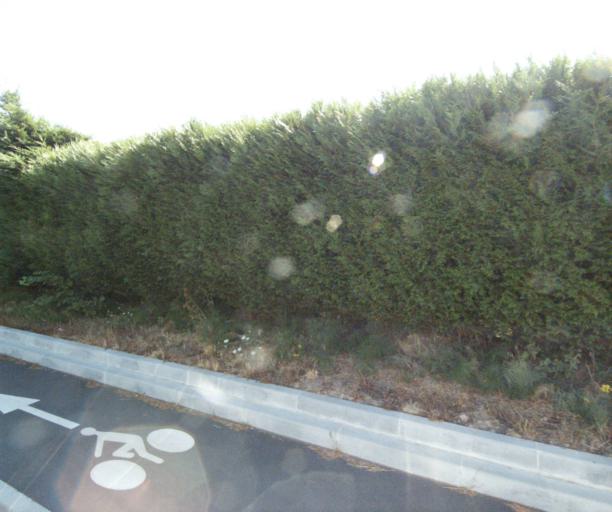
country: FR
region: Nord-Pas-de-Calais
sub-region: Departement du Nord
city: Halluin
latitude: 50.7743
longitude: 3.1120
